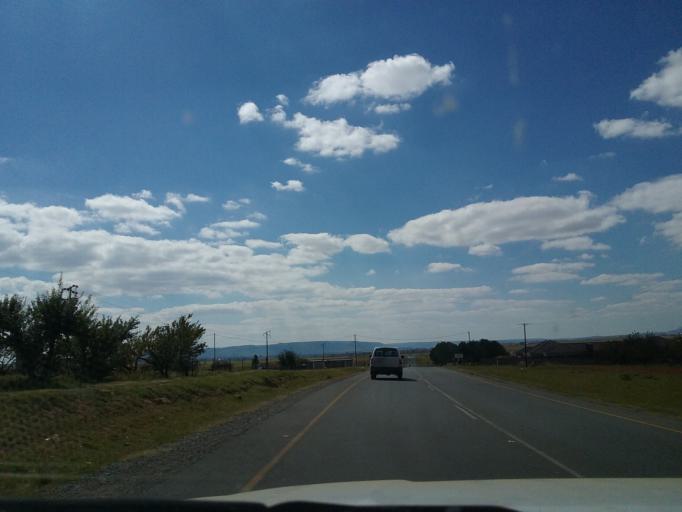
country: LS
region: Maseru
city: Maseru
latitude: -29.4815
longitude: 27.5272
